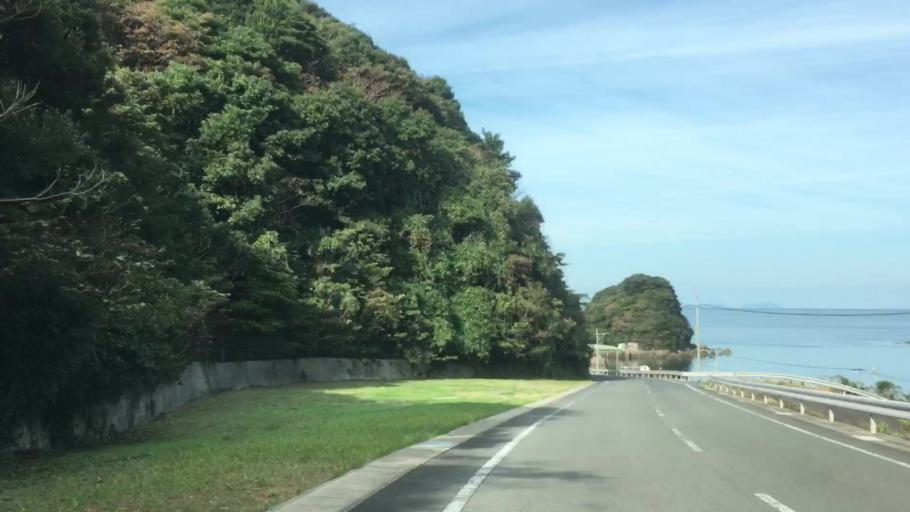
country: JP
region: Nagasaki
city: Sasebo
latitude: 33.0073
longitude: 129.5649
